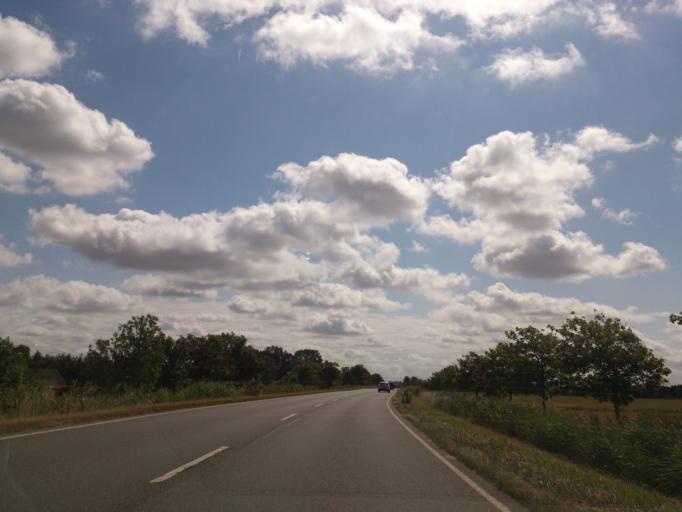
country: DE
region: Schleswig-Holstein
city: Grothusenkoog
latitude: 54.3059
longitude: 8.7563
